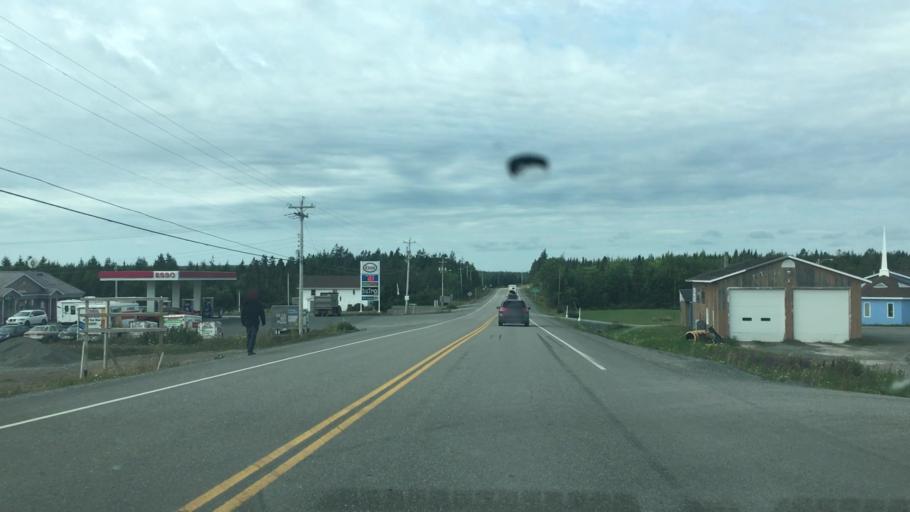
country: CA
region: Nova Scotia
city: Princeville
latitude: 45.6837
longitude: -60.7655
